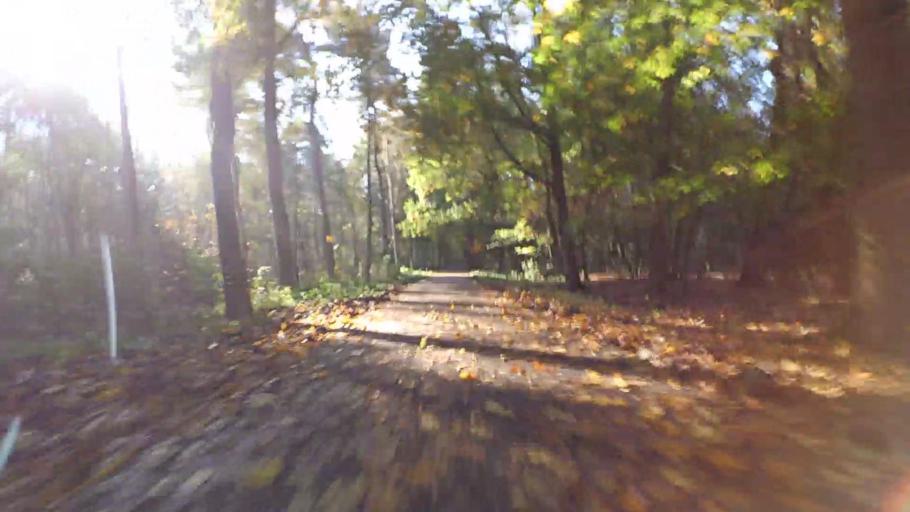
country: NL
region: Gelderland
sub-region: Gemeente Harderwijk
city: Harderwijk
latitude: 52.3309
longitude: 5.6605
